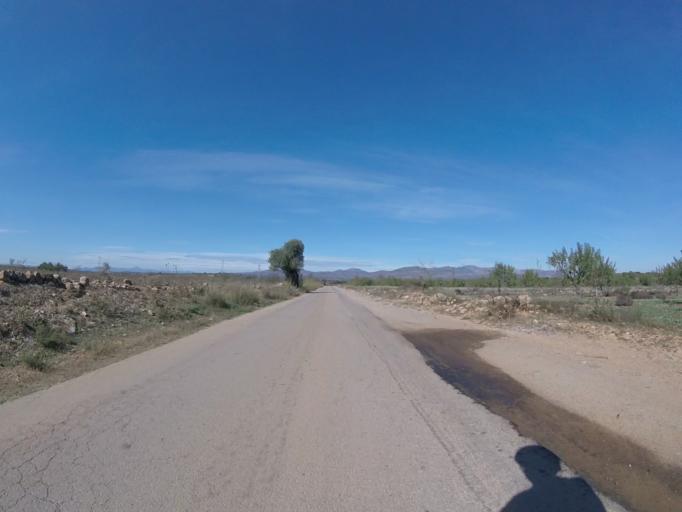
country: ES
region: Valencia
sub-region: Provincia de Castello
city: Benlloch
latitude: 40.2067
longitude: 0.0472
